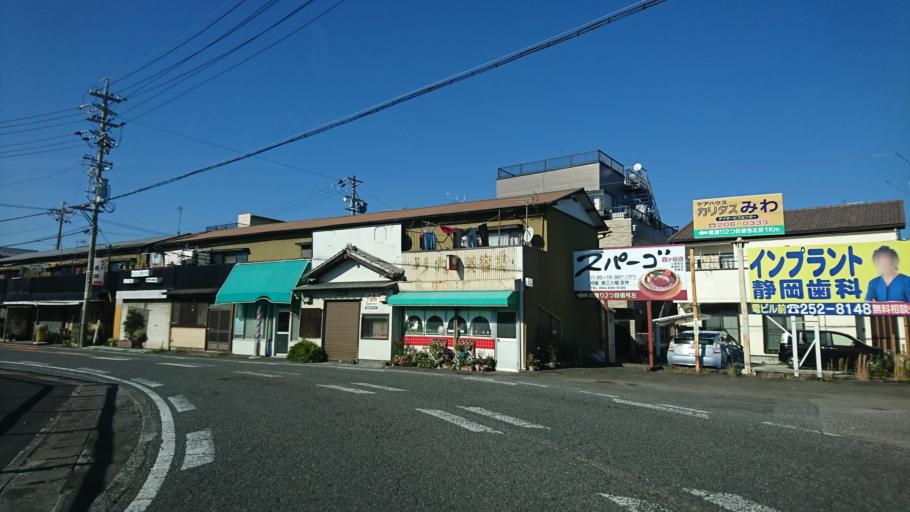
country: JP
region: Shizuoka
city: Shizuoka-shi
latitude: 35.0032
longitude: 138.3646
